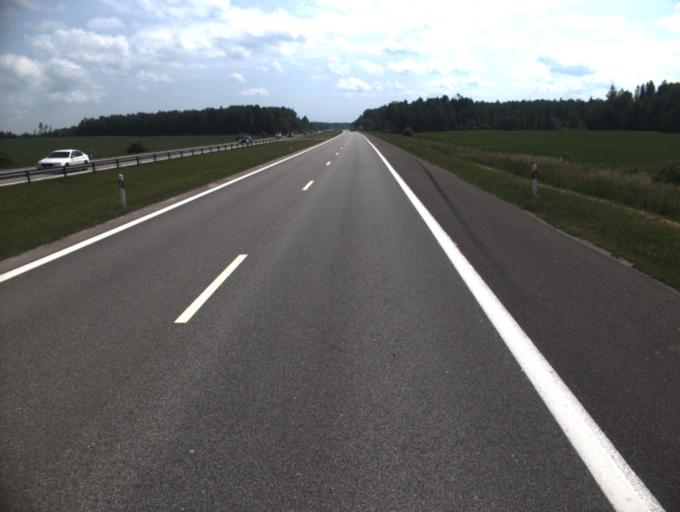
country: LT
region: Klaipedos apskritis
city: Gargzdai
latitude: 55.6983
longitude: 21.6340
